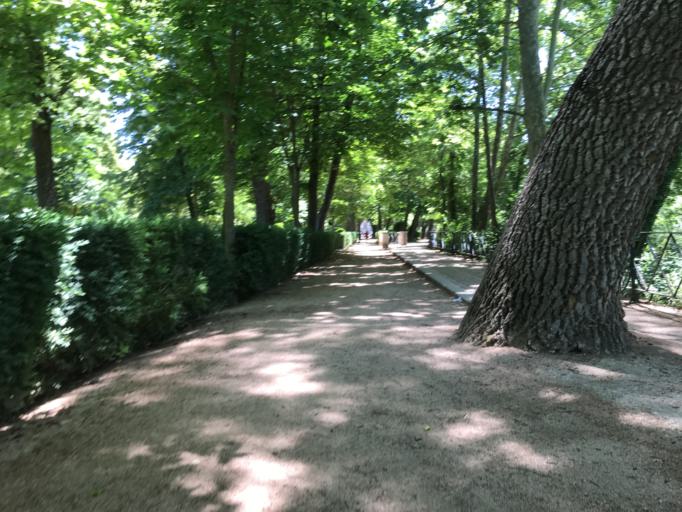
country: ES
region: Madrid
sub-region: Provincia de Madrid
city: Aranjuez
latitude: 40.0385
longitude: -3.6108
